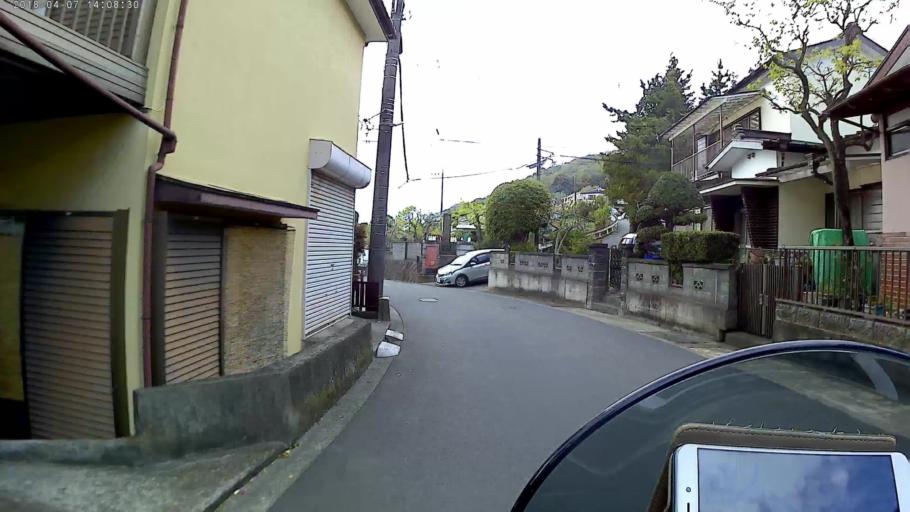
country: JP
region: Kanagawa
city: Hadano
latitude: 35.3665
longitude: 139.2457
